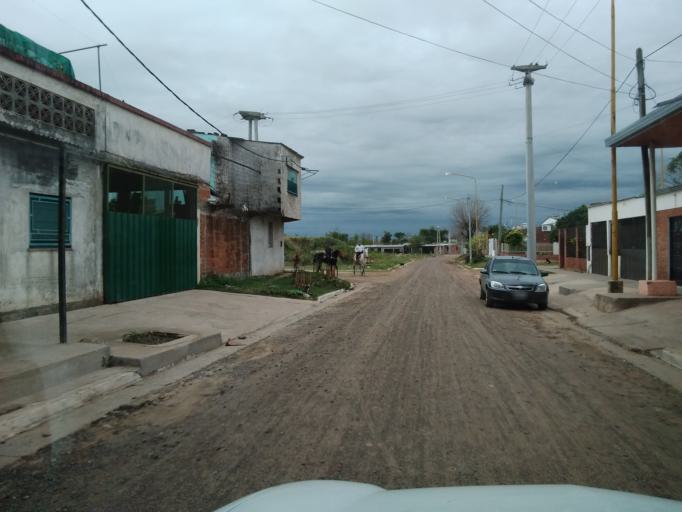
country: AR
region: Corrientes
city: Corrientes
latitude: -27.5017
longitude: -58.8044
